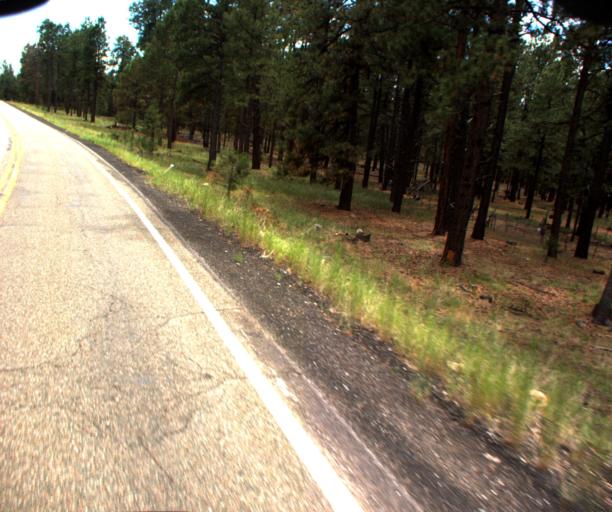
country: US
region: Arizona
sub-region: Coconino County
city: Flagstaff
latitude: 35.2963
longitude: -111.7656
